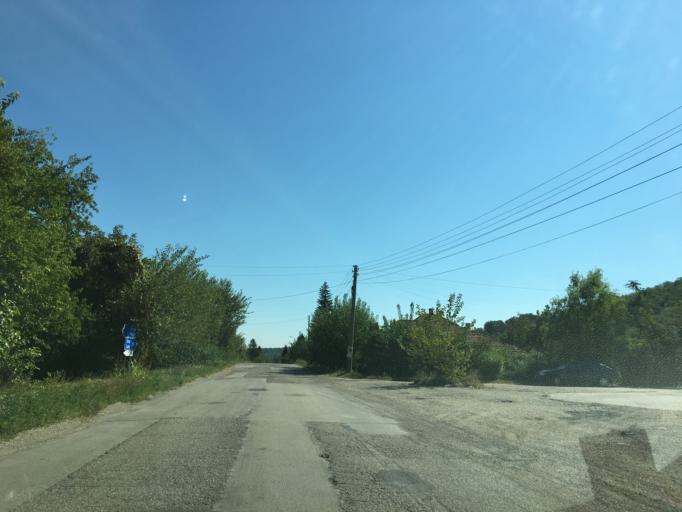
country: RO
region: Dolj
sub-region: Comuna Desa
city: Desa
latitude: 43.7701
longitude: 22.9988
